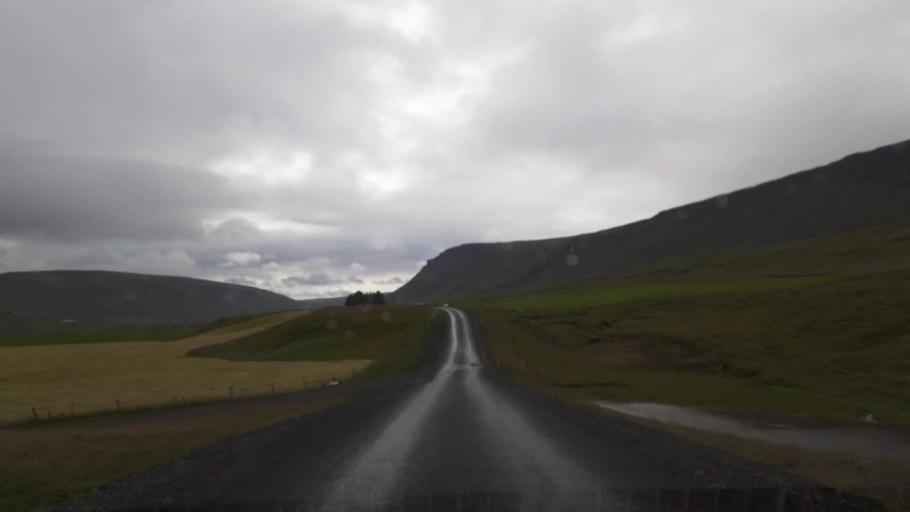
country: IS
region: East
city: Egilsstadir
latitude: 65.6188
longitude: -15.0906
